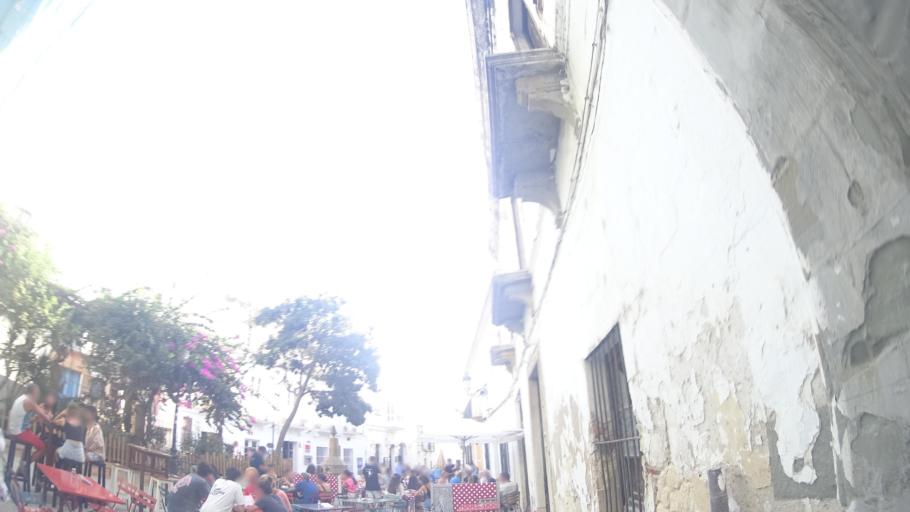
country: ES
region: Andalusia
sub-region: Provincia de Cadiz
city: Tarifa
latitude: 36.0126
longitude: -5.6018
